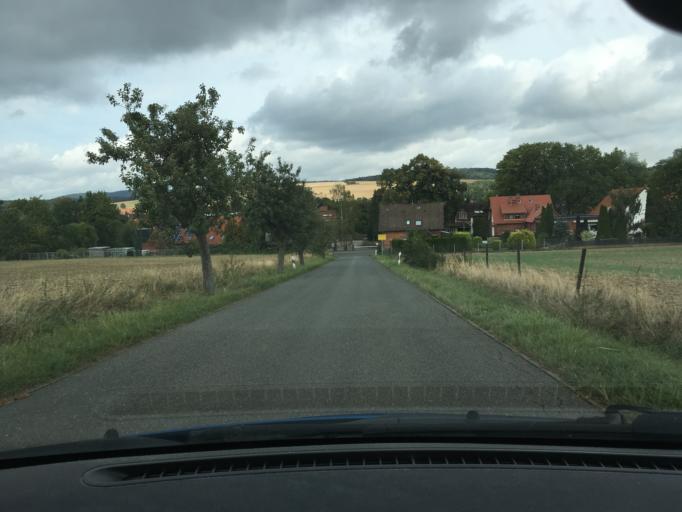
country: DE
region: Lower Saxony
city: Messenkamp
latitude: 52.2316
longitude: 9.4166
